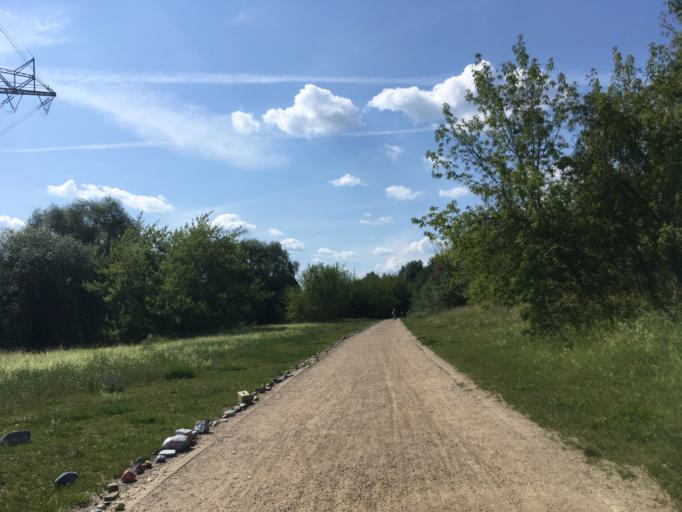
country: DE
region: Berlin
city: Marzahn
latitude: 52.5561
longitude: 13.5864
